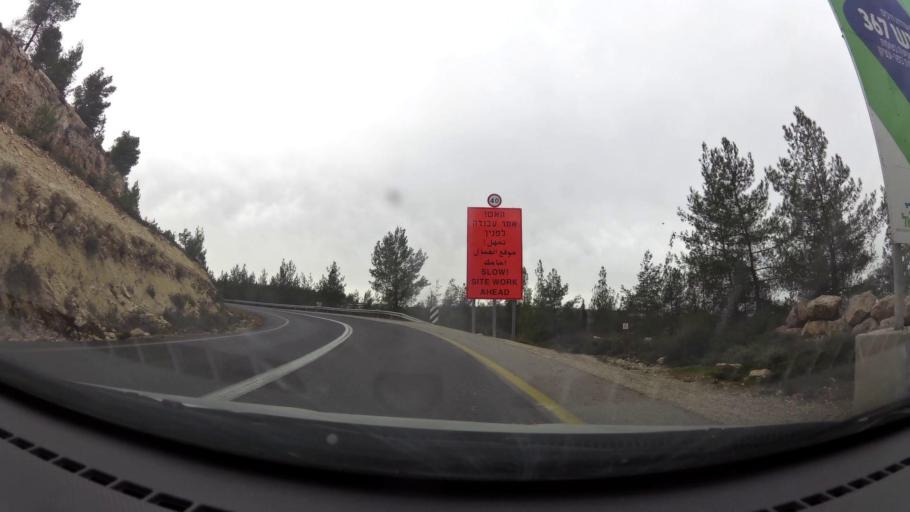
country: PS
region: West Bank
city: Nahhalin
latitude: 31.6611
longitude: 35.1146
